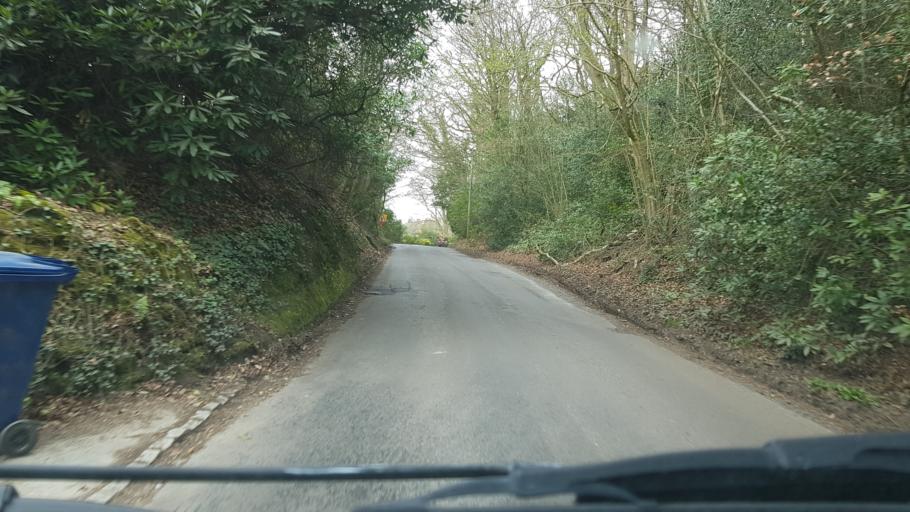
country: GB
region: England
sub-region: Surrey
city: Cranleigh
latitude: 51.1674
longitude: -0.4519
